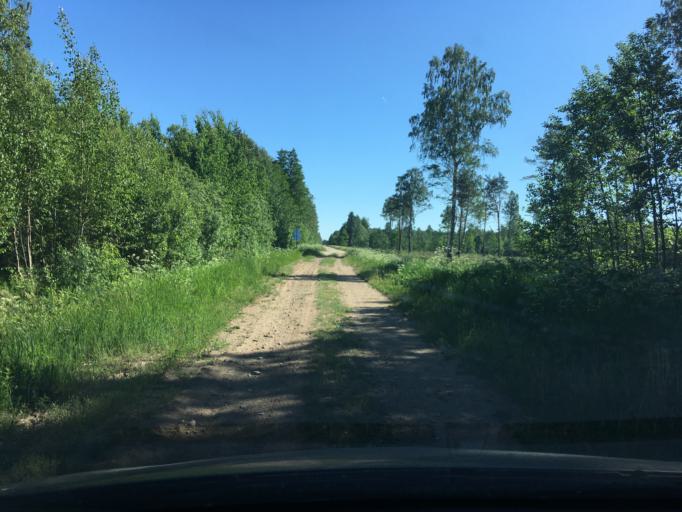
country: EE
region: Laeaene
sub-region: Lihula vald
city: Lihula
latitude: 58.6358
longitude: 23.7538
